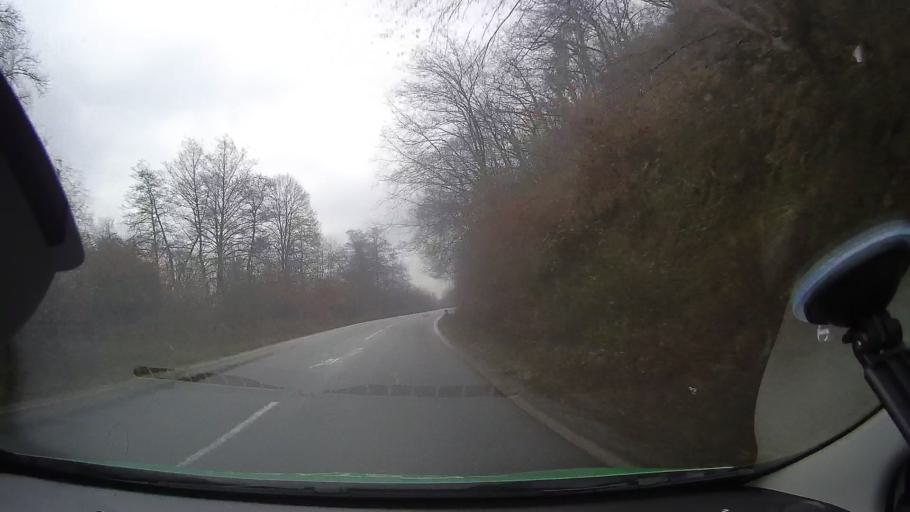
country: RO
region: Arad
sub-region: Comuna Almas
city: Almas
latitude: 46.3018
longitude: 22.1990
